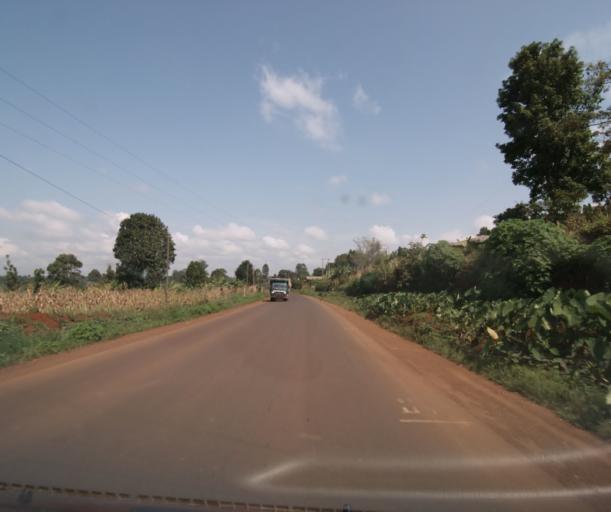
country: CM
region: West
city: Bansoa
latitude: 5.4991
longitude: 10.2497
